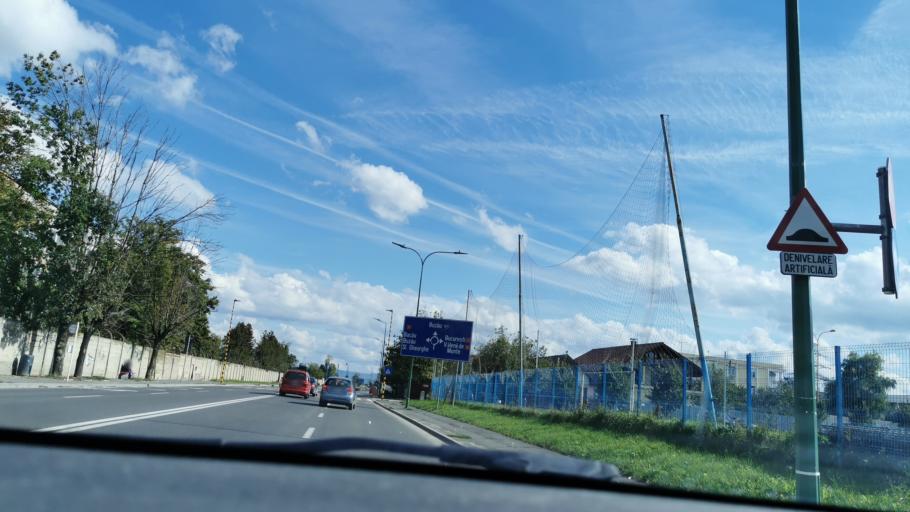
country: RO
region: Brasov
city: Brasov
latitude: 45.6492
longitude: 25.6510
